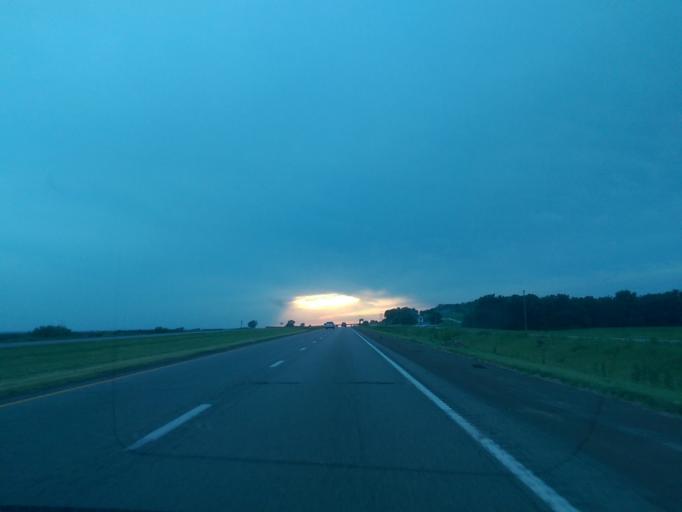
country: US
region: Missouri
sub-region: Holt County
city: Mound City
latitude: 40.1548
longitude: -95.2612
